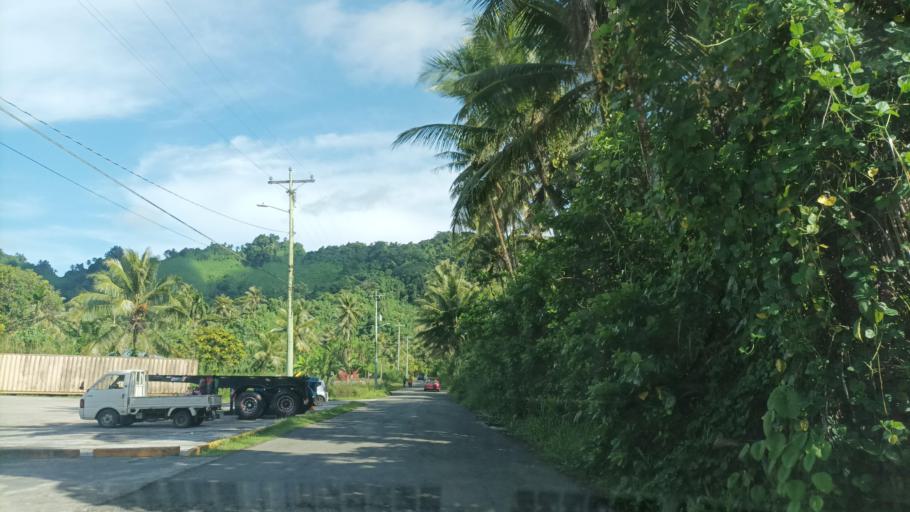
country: FM
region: Kosrae
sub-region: Lelu Municipality
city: Tofol
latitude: 5.3180
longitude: 163.0183
